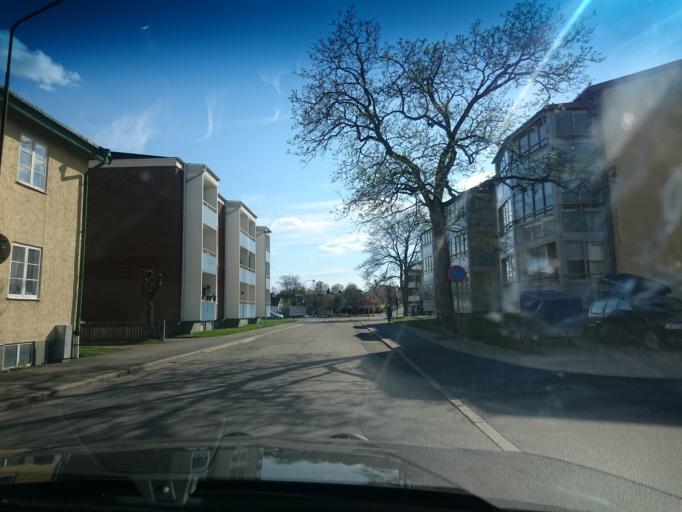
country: SE
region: Joenkoeping
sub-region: Vetlanda Kommun
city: Vetlanda
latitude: 57.4289
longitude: 15.0801
